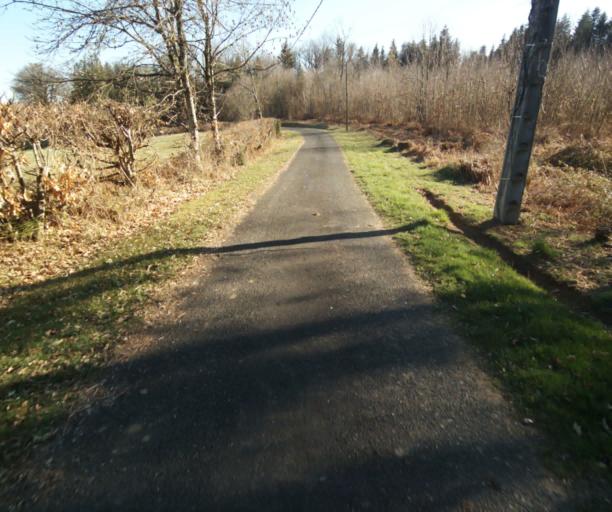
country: FR
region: Limousin
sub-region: Departement de la Correze
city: Seilhac
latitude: 45.3870
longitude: 1.6982
